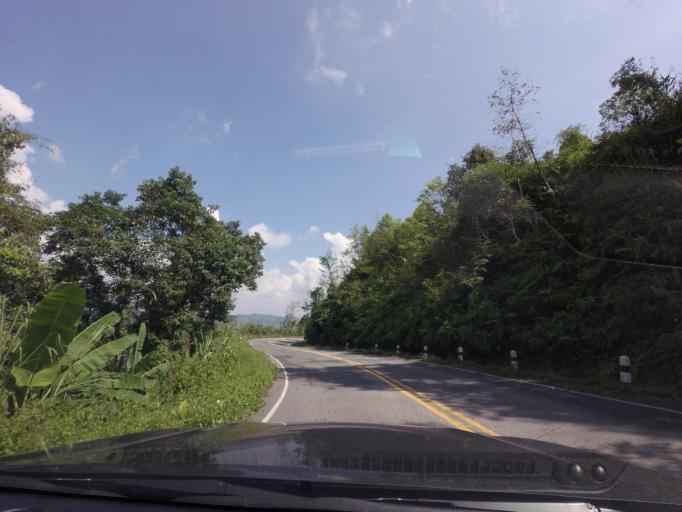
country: TH
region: Nan
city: Bo Kluea
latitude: 19.0537
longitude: 101.0909
